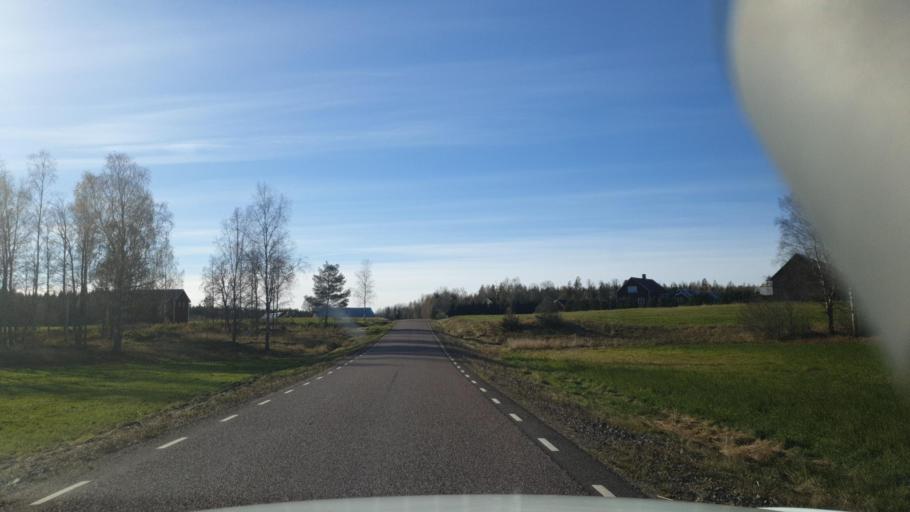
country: SE
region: Vaermland
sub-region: Karlstads Kommun
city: Edsvalla
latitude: 59.4900
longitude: 13.0962
